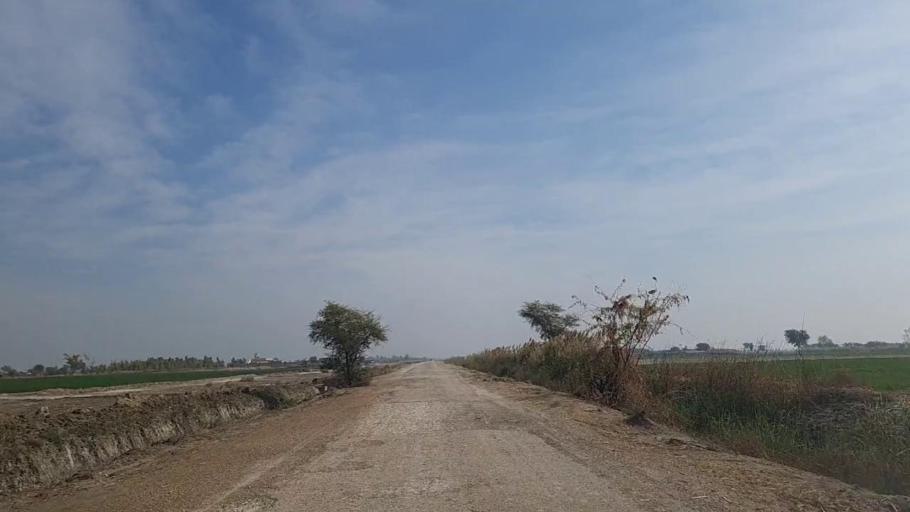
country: PK
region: Sindh
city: Nawabshah
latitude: 26.3319
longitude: 68.4505
